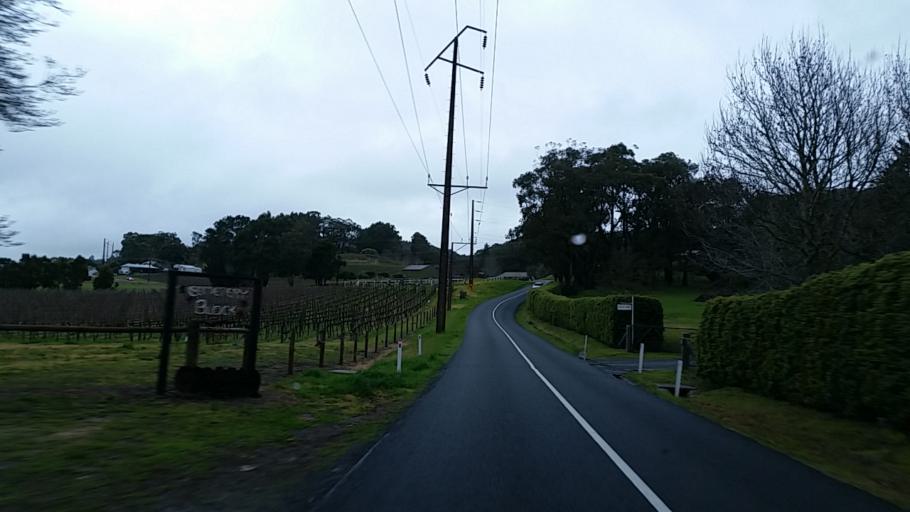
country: AU
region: South Australia
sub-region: Adelaide Hills
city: Bridgewater
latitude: -34.9721
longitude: 138.7373
